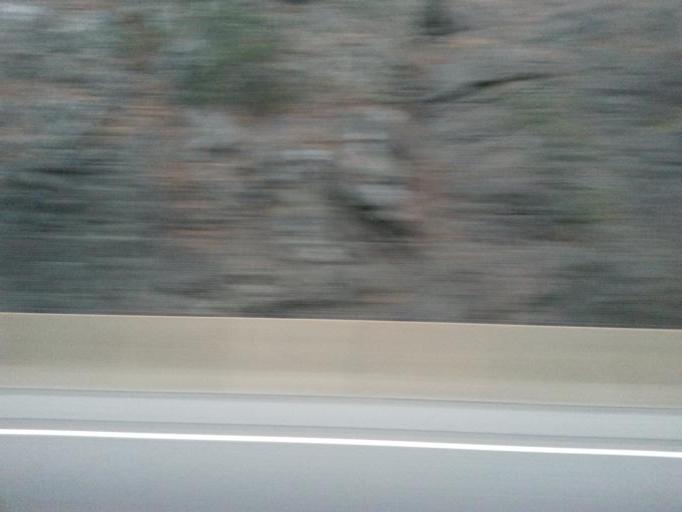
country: US
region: North Carolina
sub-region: Haywood County
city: Cove Creek
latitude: 35.7582
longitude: -83.0714
